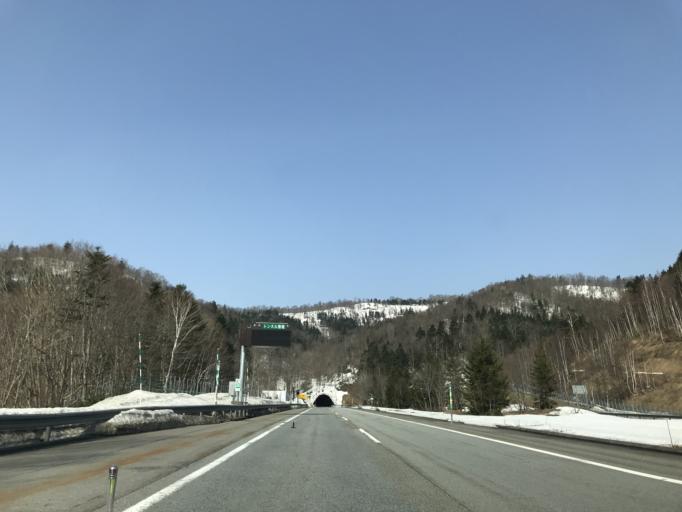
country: JP
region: Hokkaido
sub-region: Asahikawa-shi
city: Asahikawa
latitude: 43.7922
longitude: 142.2683
